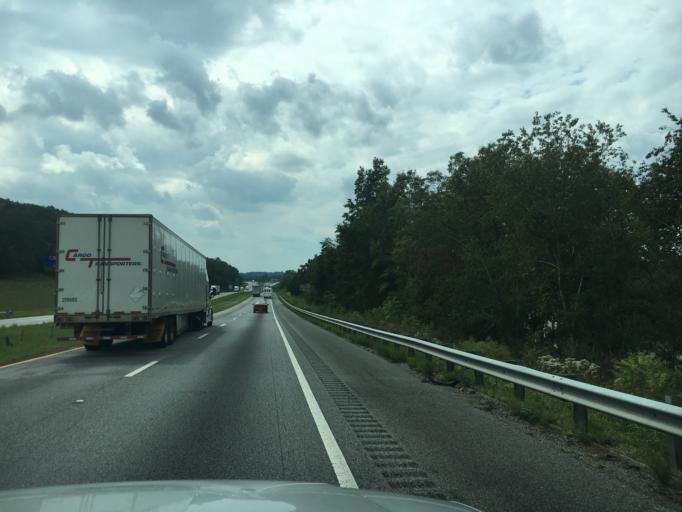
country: US
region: Georgia
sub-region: Franklin County
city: Gumlog
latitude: 34.4954
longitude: -83.0094
